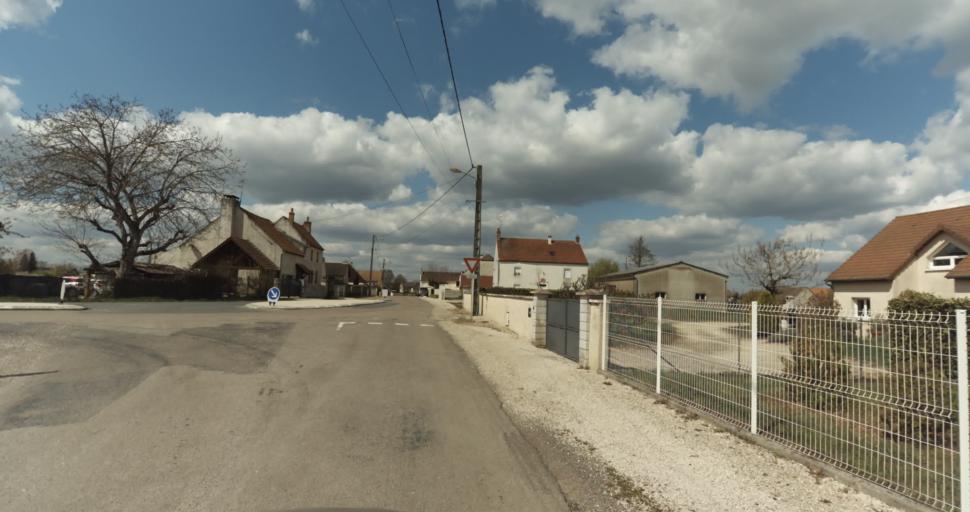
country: FR
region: Bourgogne
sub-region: Departement de la Cote-d'Or
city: Auxonne
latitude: 47.1885
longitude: 5.4032
